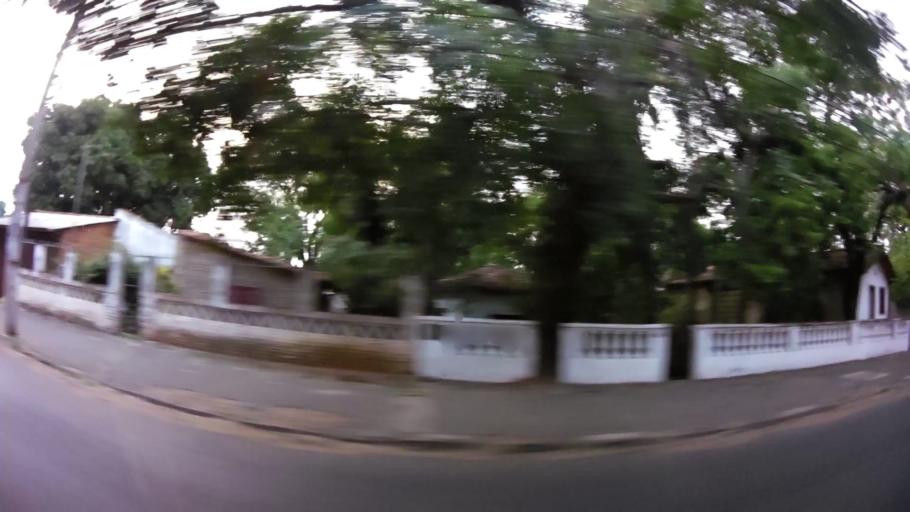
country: PY
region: Central
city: Lambare
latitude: -25.3322
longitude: -57.6202
